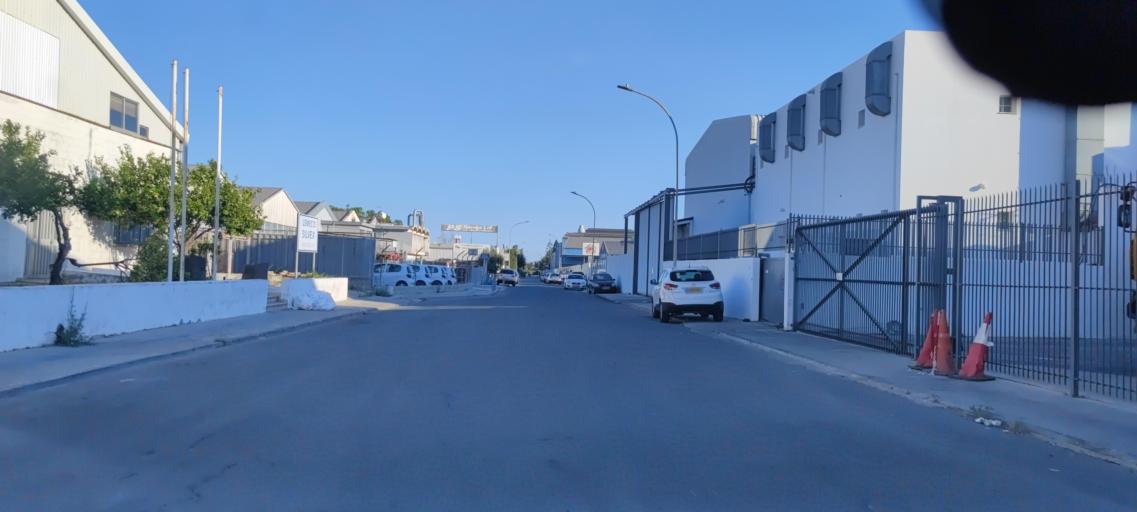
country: CY
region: Limassol
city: Pano Polemidia
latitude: 34.6729
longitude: 32.9963
